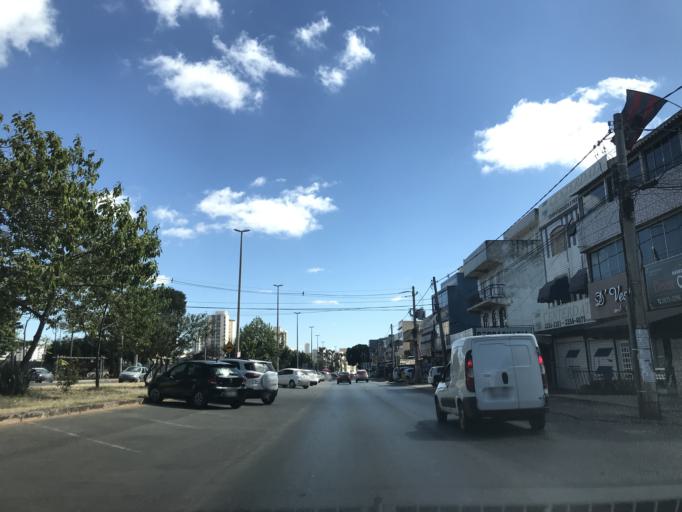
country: BR
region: Federal District
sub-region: Brasilia
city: Brasilia
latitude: -15.8606
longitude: -48.0271
